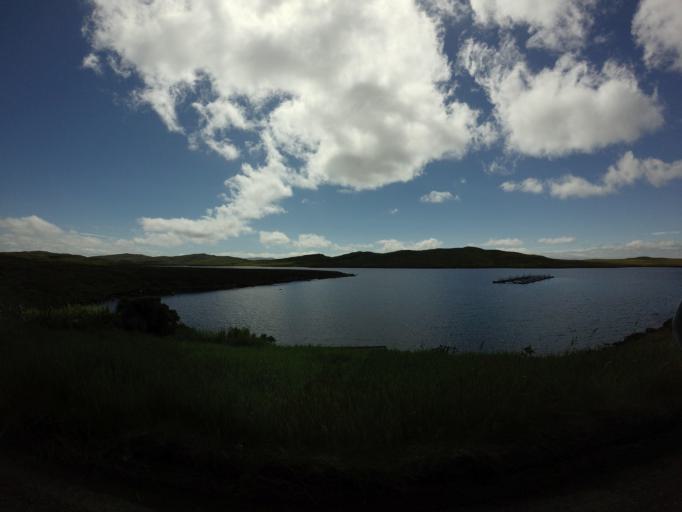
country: GB
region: Scotland
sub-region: Eilean Siar
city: Stornoway
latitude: 58.1595
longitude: -6.5293
